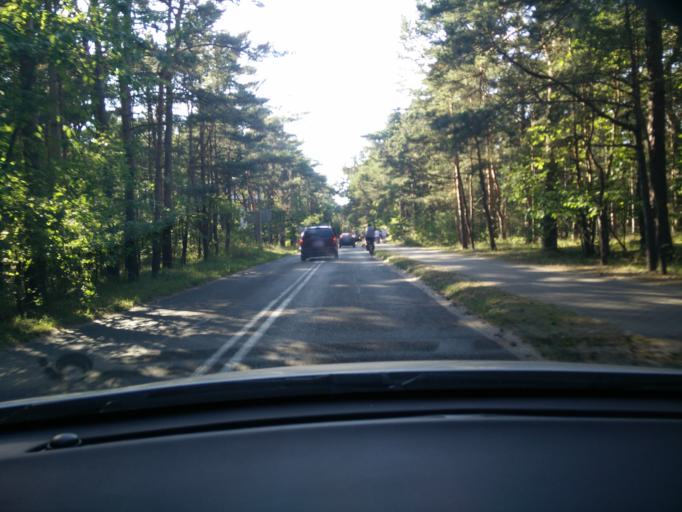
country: PL
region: Pomeranian Voivodeship
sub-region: Powiat pucki
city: Jastarnia
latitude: 54.6779
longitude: 18.7235
